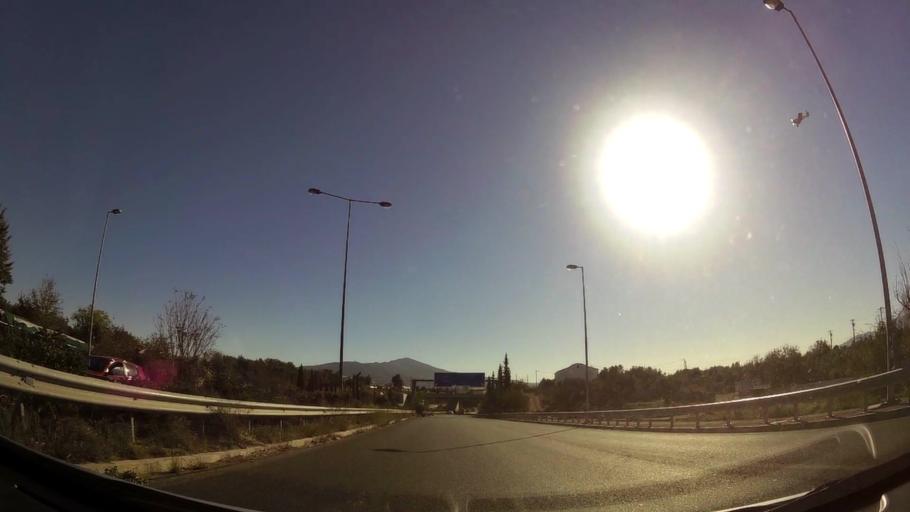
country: GR
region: Attica
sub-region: Nomarchia Athinas
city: Lykovrysi
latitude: 38.0965
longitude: 23.7727
